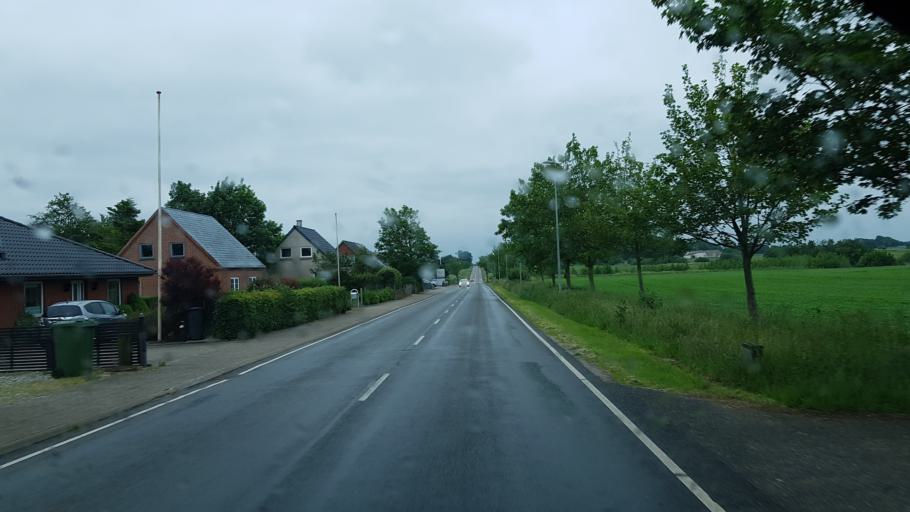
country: DK
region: South Denmark
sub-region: Vejen Kommune
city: Holsted
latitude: 55.5533
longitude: 8.8235
